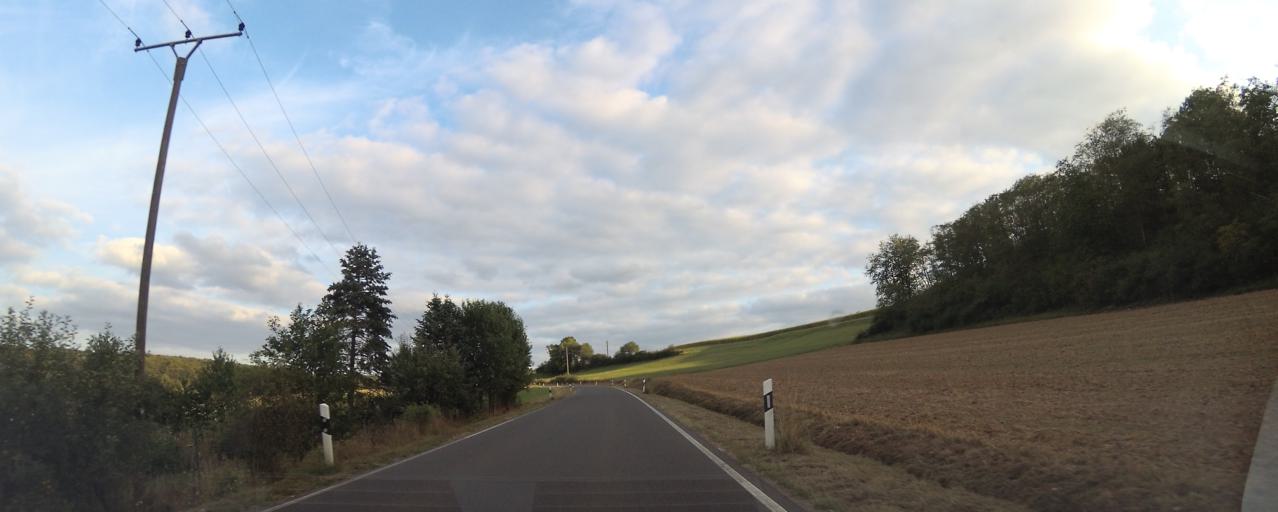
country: DE
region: Rheinland-Pfalz
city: Beilingen
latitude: 49.9619
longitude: 6.6661
